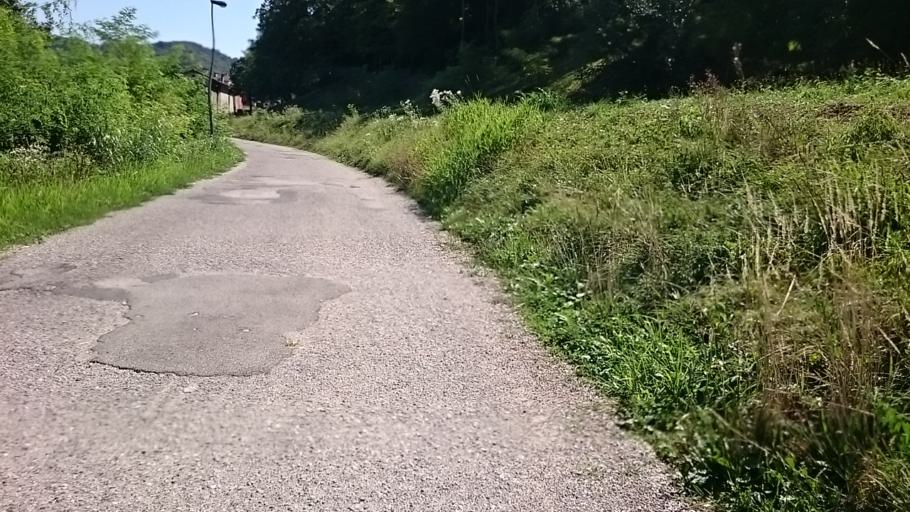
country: IT
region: Veneto
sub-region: Provincia di Treviso
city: Follina
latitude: 45.9402
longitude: 12.1256
